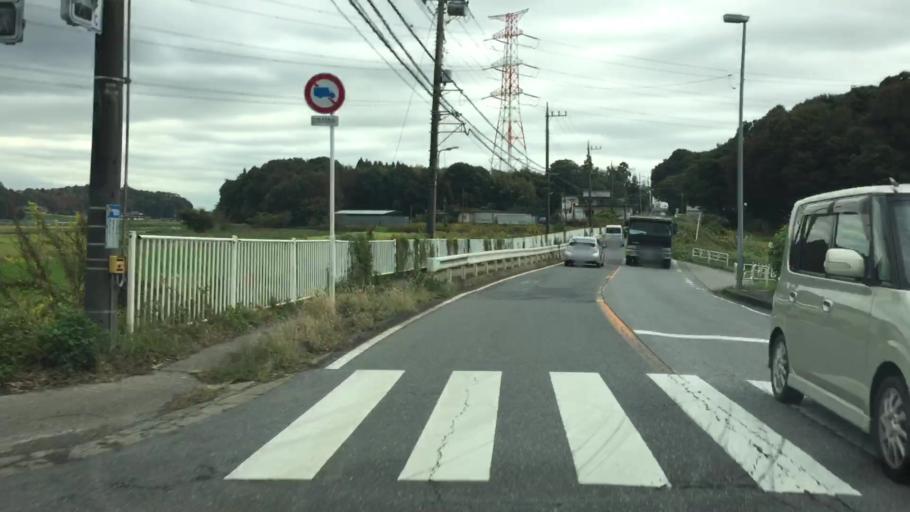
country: JP
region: Chiba
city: Abiko
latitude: 35.8428
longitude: 140.0306
